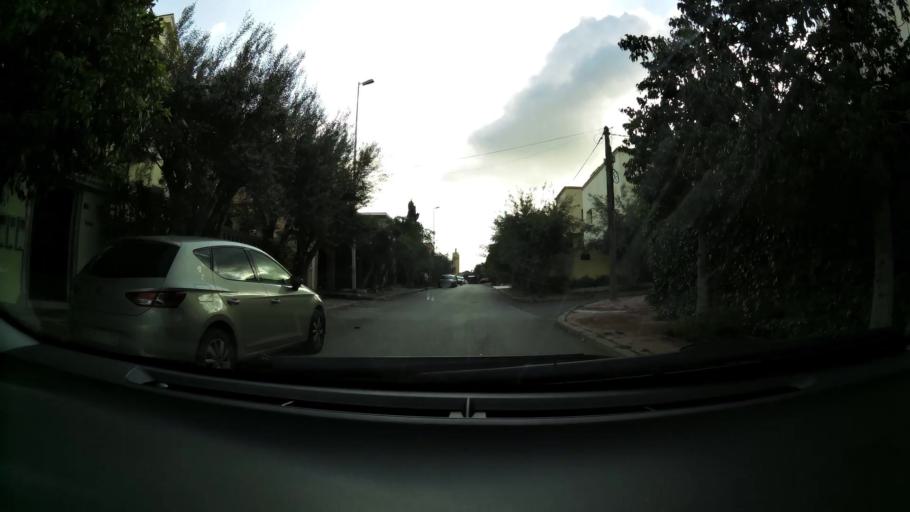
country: MA
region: Chaouia-Ouardigha
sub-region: Settat Province
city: Settat
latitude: 33.0092
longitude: -7.6345
